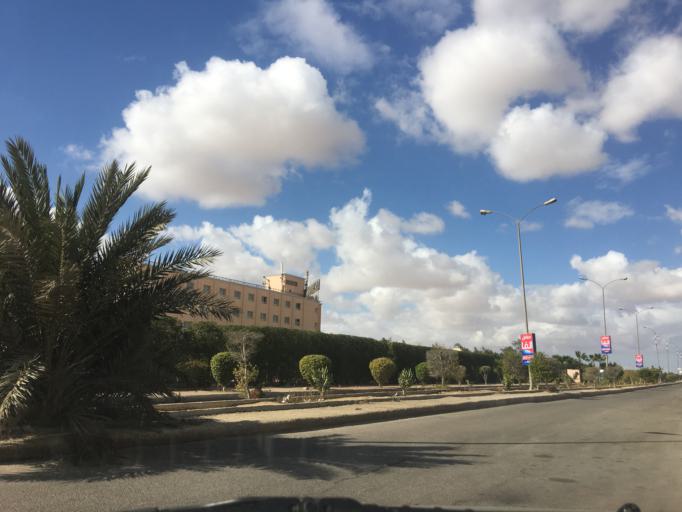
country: EG
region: Al Jizah
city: Madinat Sittah Uktubar
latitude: 29.9961
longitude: 30.9703
